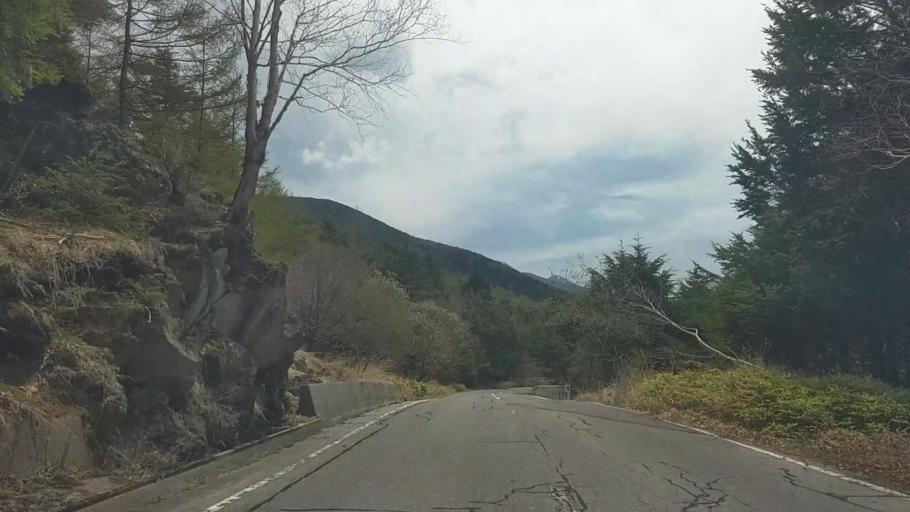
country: JP
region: Nagano
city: Chino
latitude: 36.0542
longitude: 138.3194
